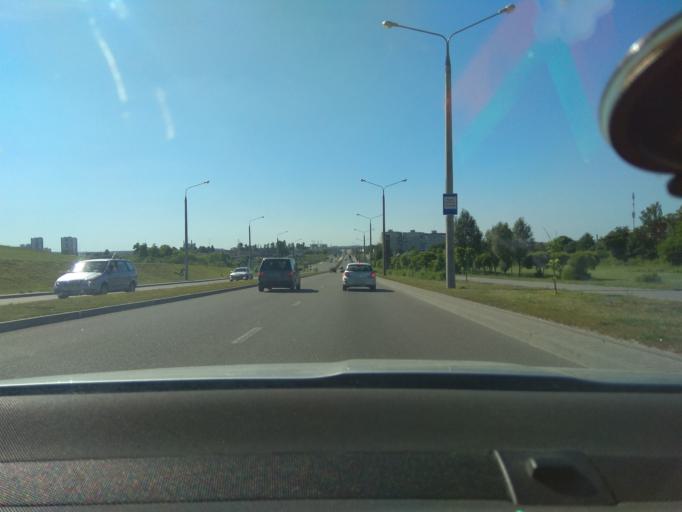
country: BY
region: Grodnenskaya
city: Hrodna
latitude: 53.6483
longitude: 23.8080
